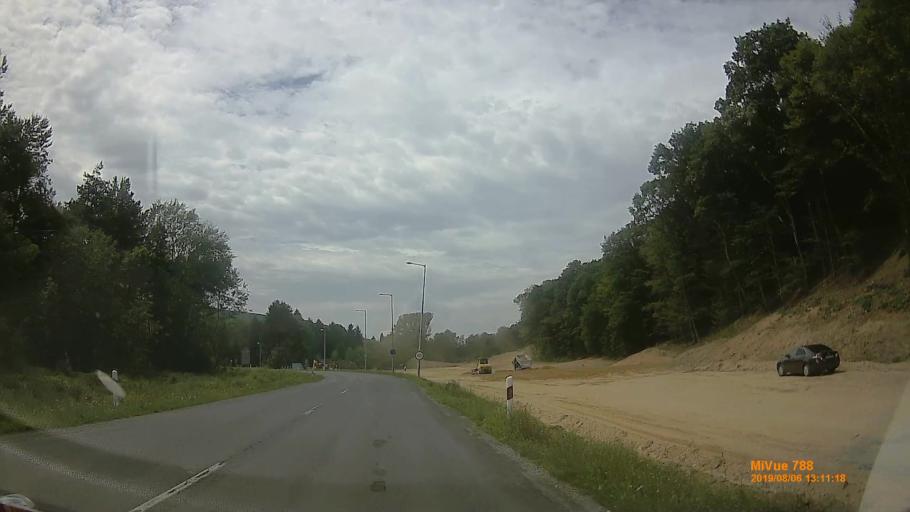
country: AT
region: Burgenland
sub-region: Politischer Bezirk Oberpullendorf
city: Mannersdorf an der Rabnitz
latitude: 47.4071
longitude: 16.5212
